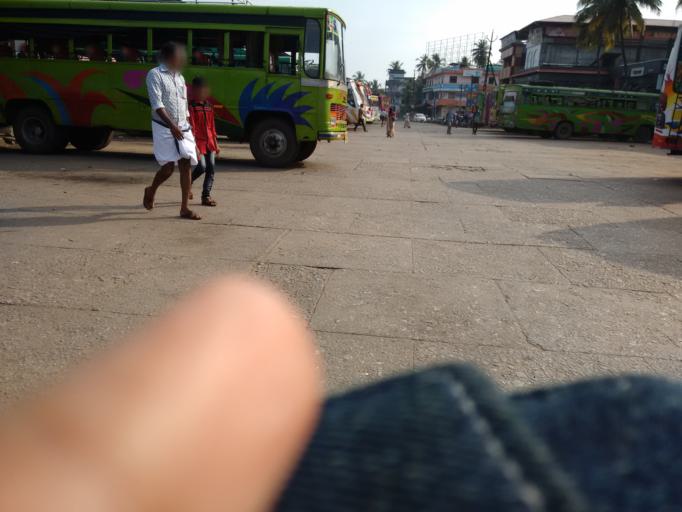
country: IN
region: Kerala
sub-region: Kozhikode
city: Badagara
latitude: 11.5948
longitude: 75.5937
